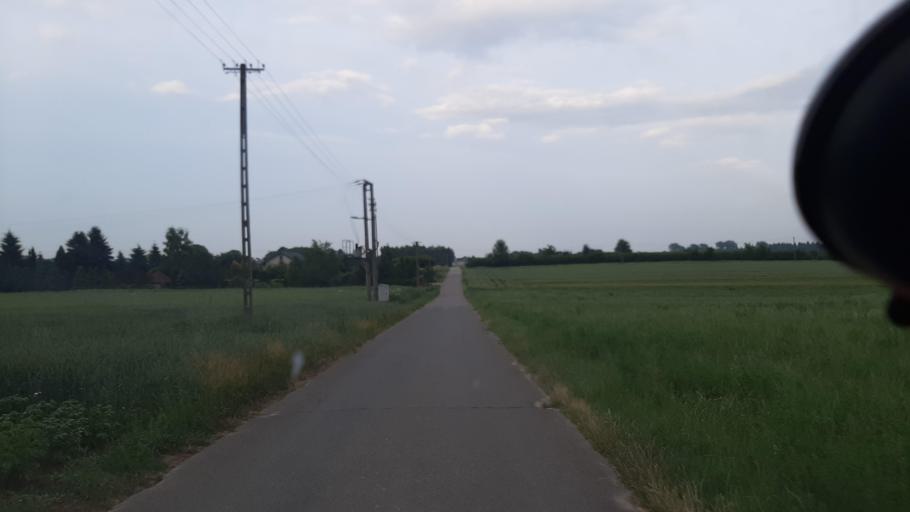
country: PL
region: Lublin Voivodeship
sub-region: Powiat lubelski
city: Garbow
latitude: 51.3532
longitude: 22.3496
